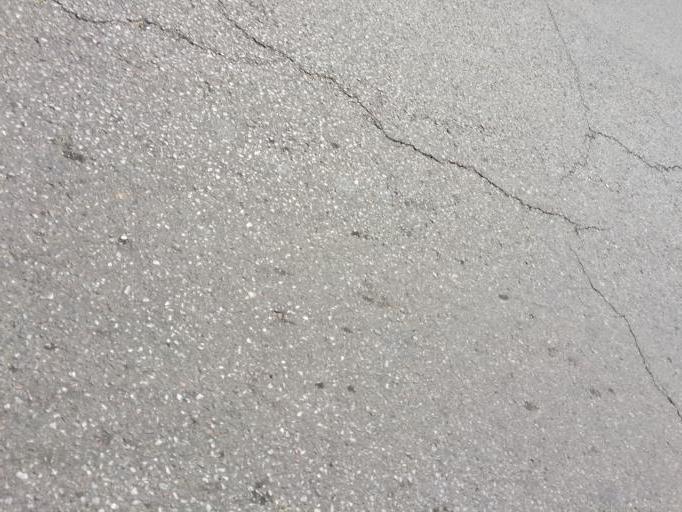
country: MX
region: Sonora
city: Hermosillo
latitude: 29.1098
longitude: -110.9661
